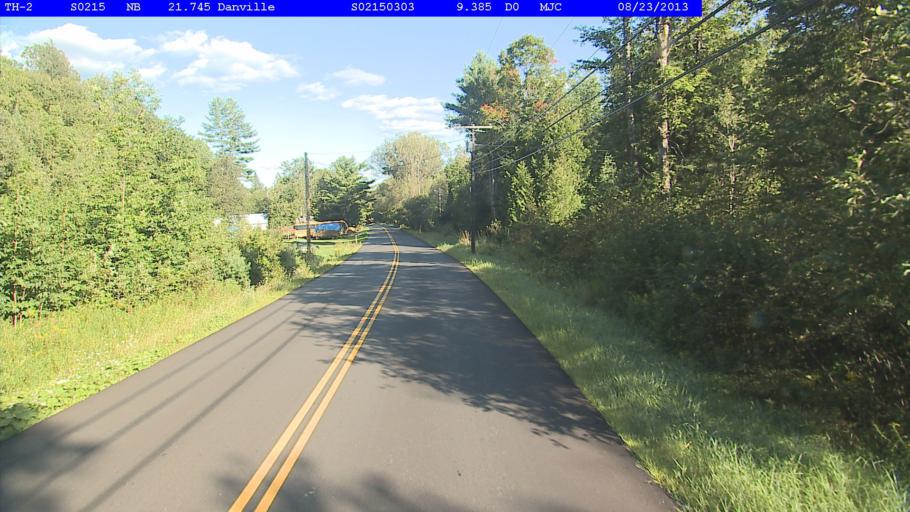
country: US
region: Vermont
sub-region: Caledonia County
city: St Johnsbury
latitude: 44.4545
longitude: -72.0762
